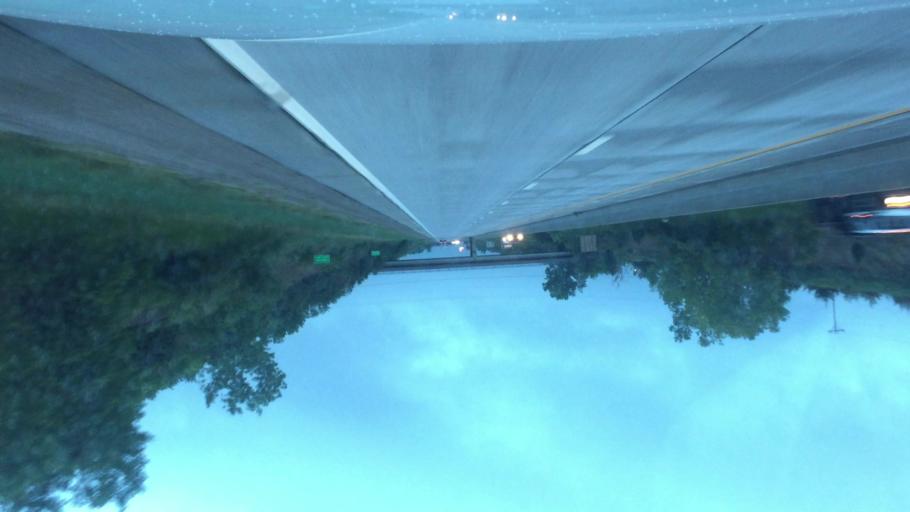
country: US
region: Kansas
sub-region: Neosho County
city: Chanute
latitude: 37.6769
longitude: -95.4796
